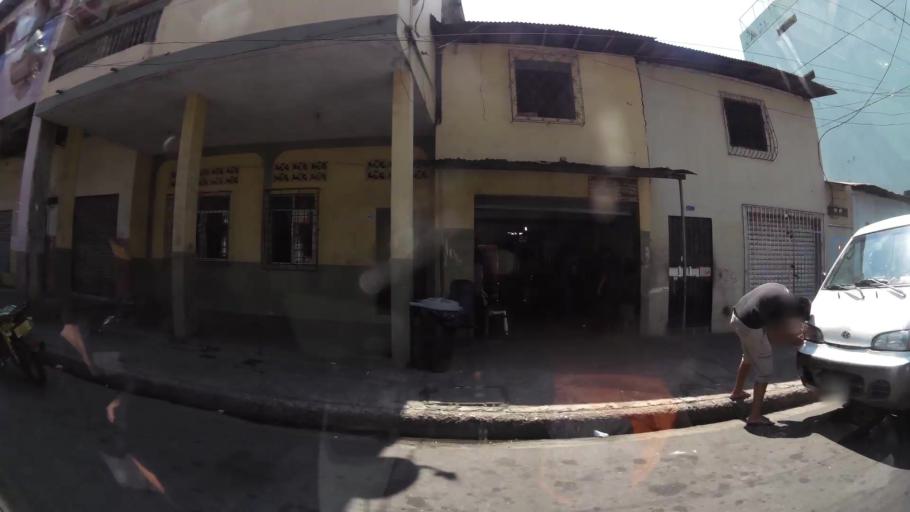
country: EC
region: Guayas
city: Guayaquil
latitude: -2.1962
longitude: -79.9120
